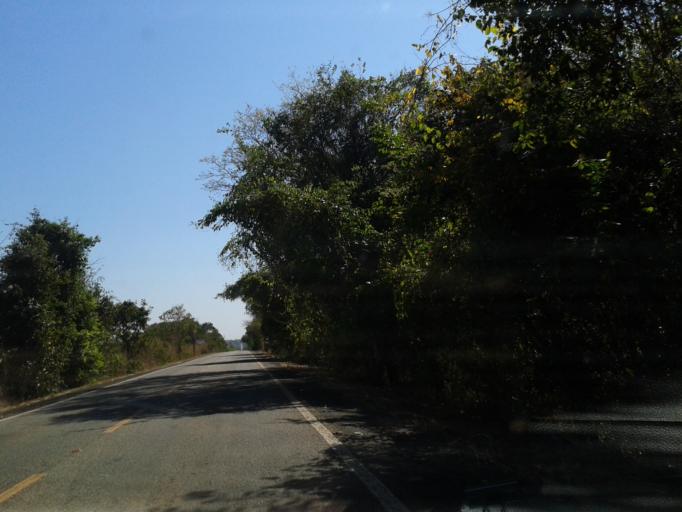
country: BR
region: Goias
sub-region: Crixas
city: Crixas
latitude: -14.0081
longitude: -50.3254
